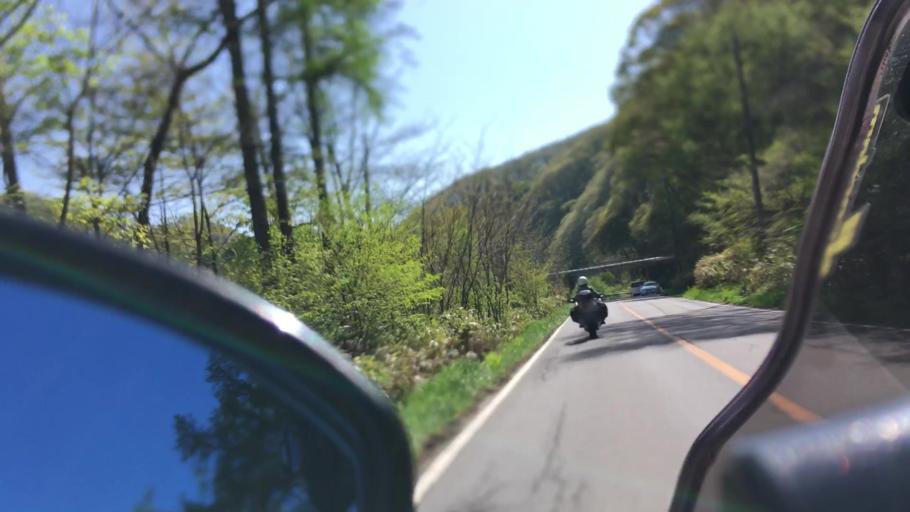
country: JP
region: Nagano
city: Komoro
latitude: 36.4914
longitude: 138.4895
